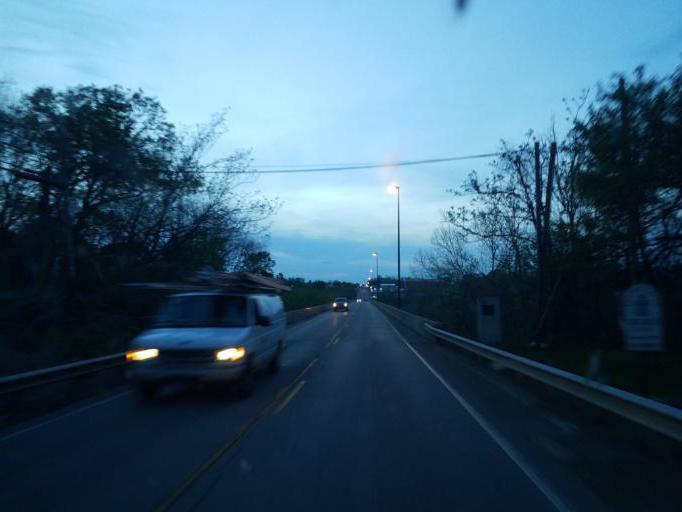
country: US
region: Kentucky
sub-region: Hart County
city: Munfordville
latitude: 37.2673
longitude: -85.8830
